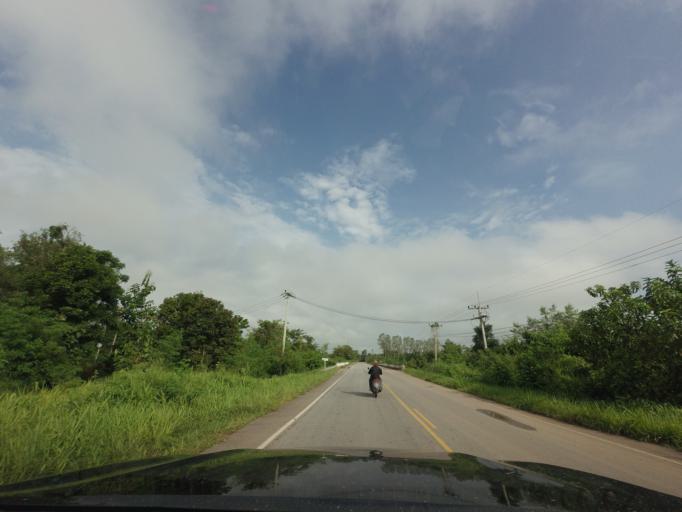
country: TH
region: Changwat Udon Thani
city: Nam Som
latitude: 17.8255
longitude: 102.2682
